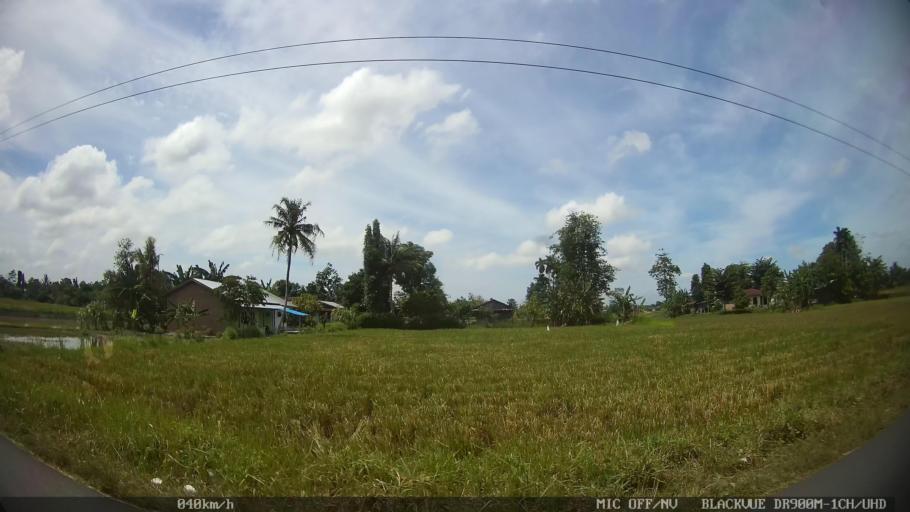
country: ID
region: North Sumatra
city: Percut
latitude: 3.5893
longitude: 98.8714
